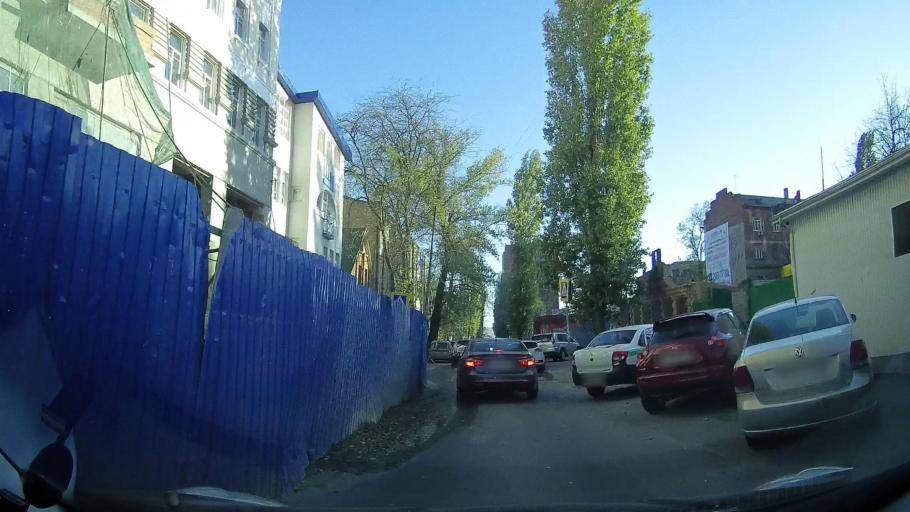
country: RU
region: Rostov
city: Rostov-na-Donu
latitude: 47.2258
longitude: 39.7367
